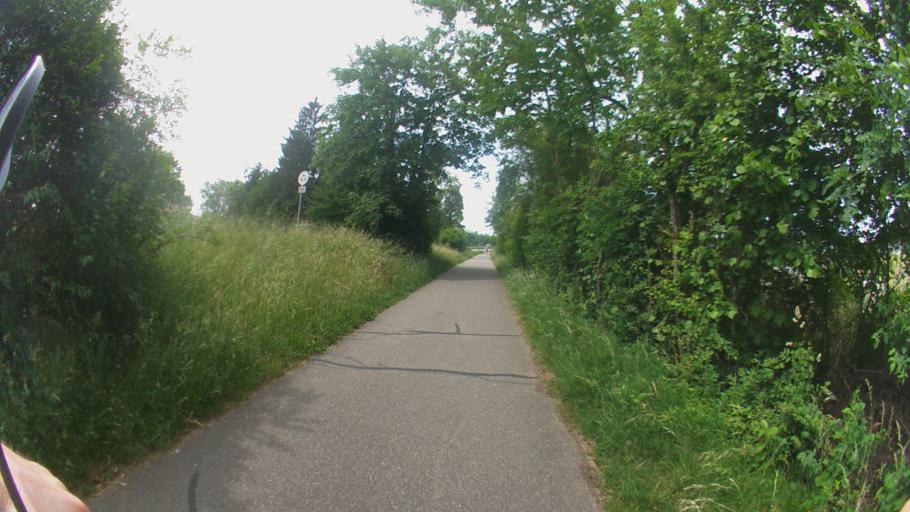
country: CH
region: Aargau
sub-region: Bezirk Zurzach
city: Klingnau
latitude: 47.5766
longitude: 8.2403
